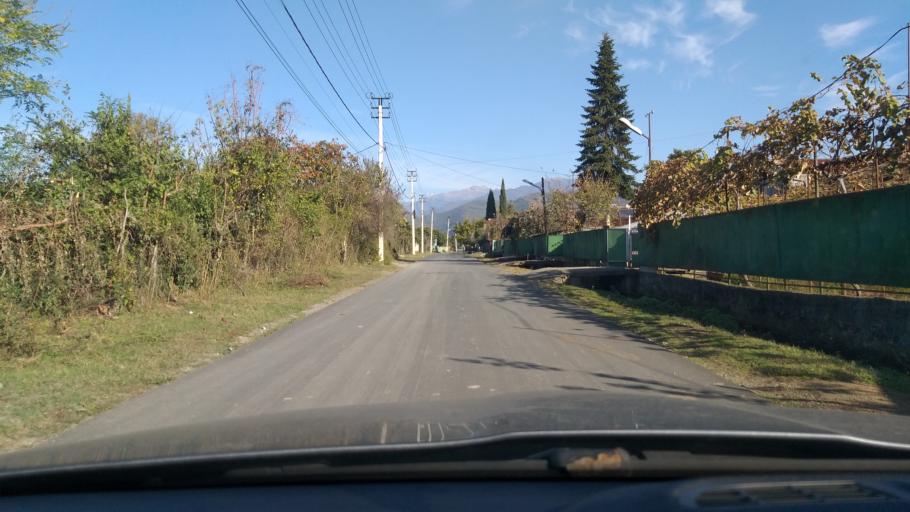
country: GE
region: Abkhazia
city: Sokhumi
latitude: 43.0170
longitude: 40.9652
